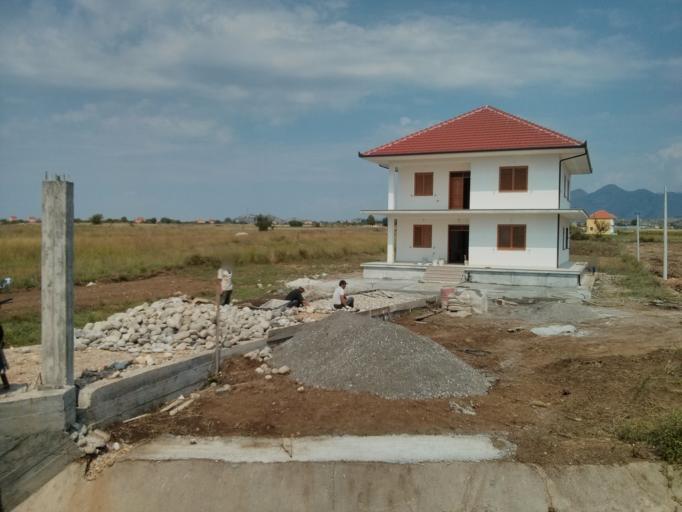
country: AL
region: Shkoder
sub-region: Rrethi i Malesia e Madhe
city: Gruemire
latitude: 42.1429
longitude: 19.5218
